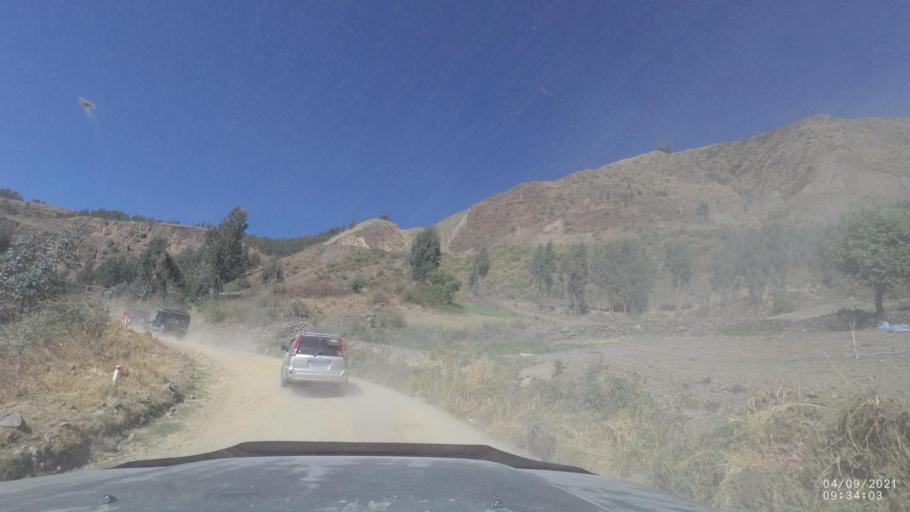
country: BO
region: Cochabamba
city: Sipe Sipe
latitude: -17.3553
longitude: -66.3789
